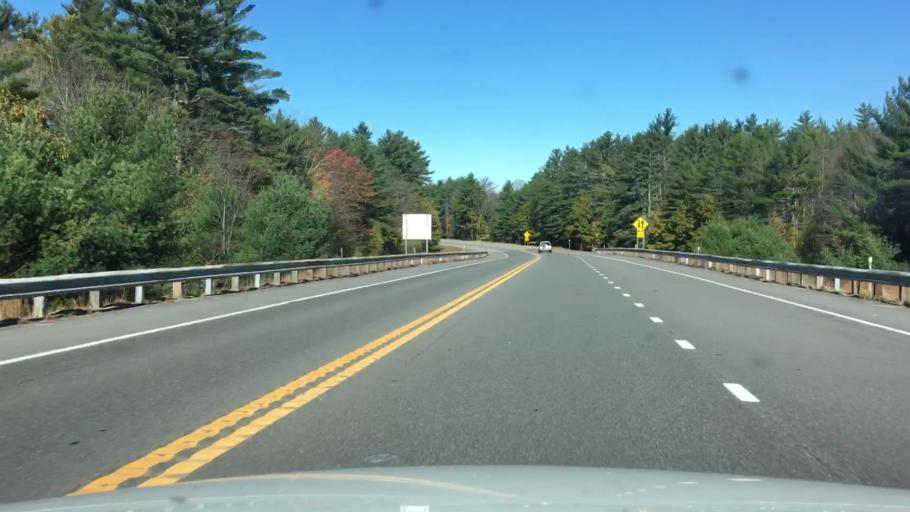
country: US
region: New Hampshire
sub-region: Carroll County
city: Sanbornville
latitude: 43.4825
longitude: -71.0057
